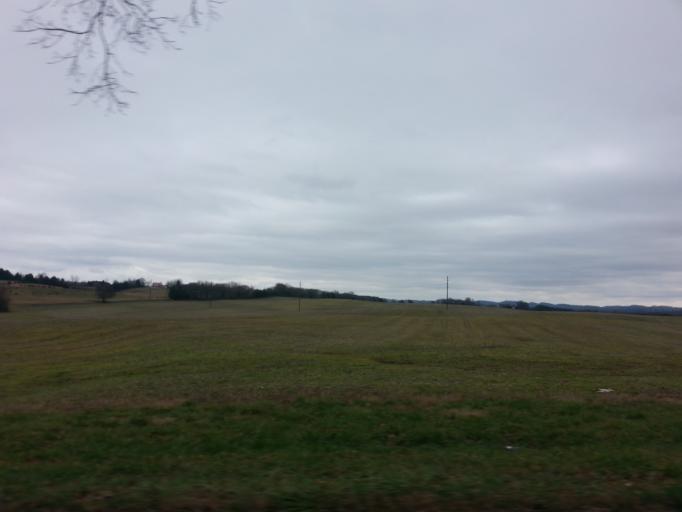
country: US
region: Tennessee
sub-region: Jefferson County
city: Jefferson City
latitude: 36.1490
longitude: -83.4733
